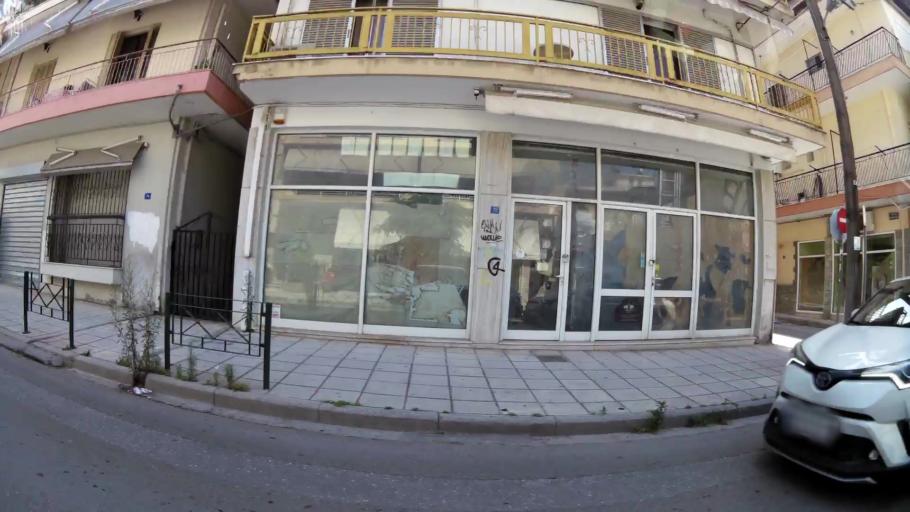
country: GR
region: Central Macedonia
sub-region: Nomos Thessalonikis
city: Evosmos
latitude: 40.6686
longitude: 22.9203
